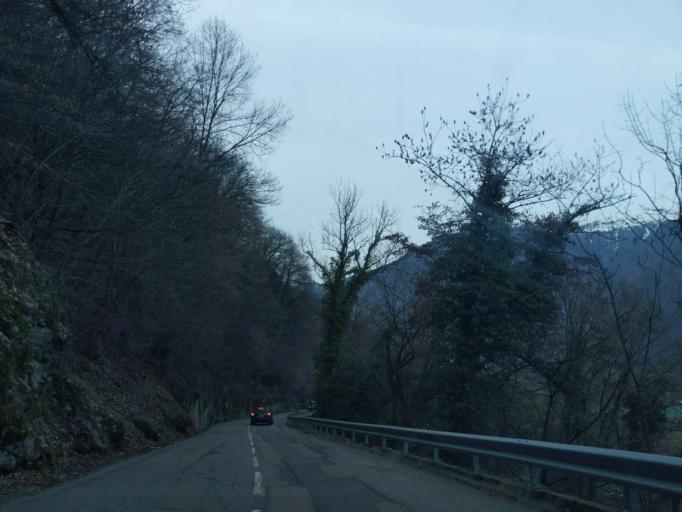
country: FR
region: Rhone-Alpes
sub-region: Departement de la Savoie
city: La Bathie
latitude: 45.6260
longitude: 6.4346
